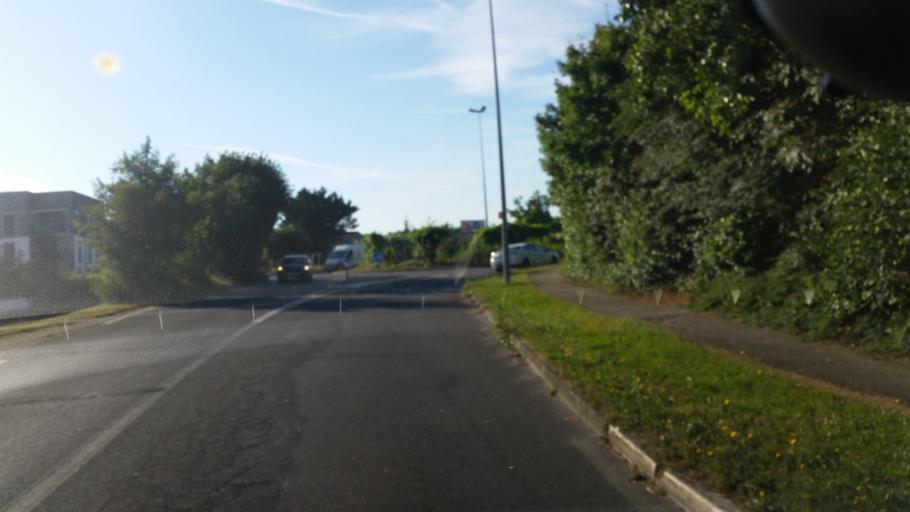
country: FR
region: Poitou-Charentes
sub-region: Departement de la Charente-Maritime
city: Puilboreau
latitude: 46.1720
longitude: -1.1082
